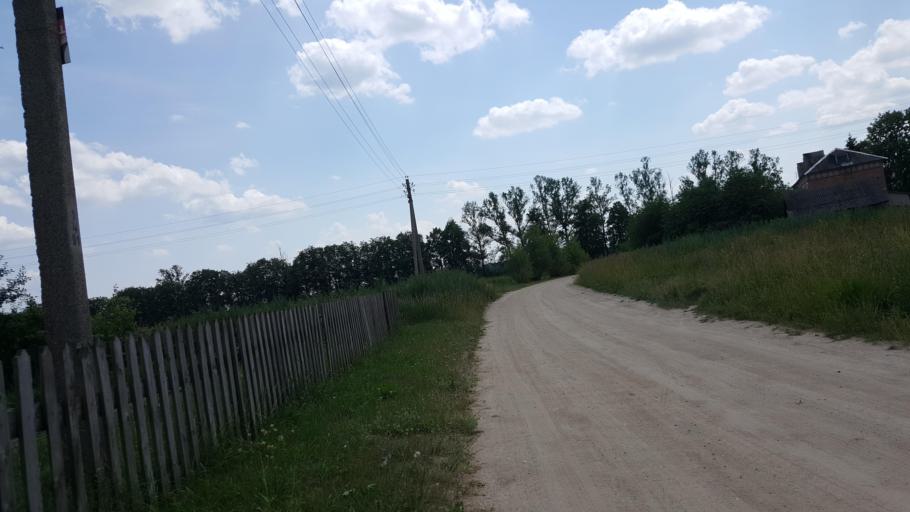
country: BY
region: Brest
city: Kamyanyets
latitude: 52.3959
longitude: 23.7650
